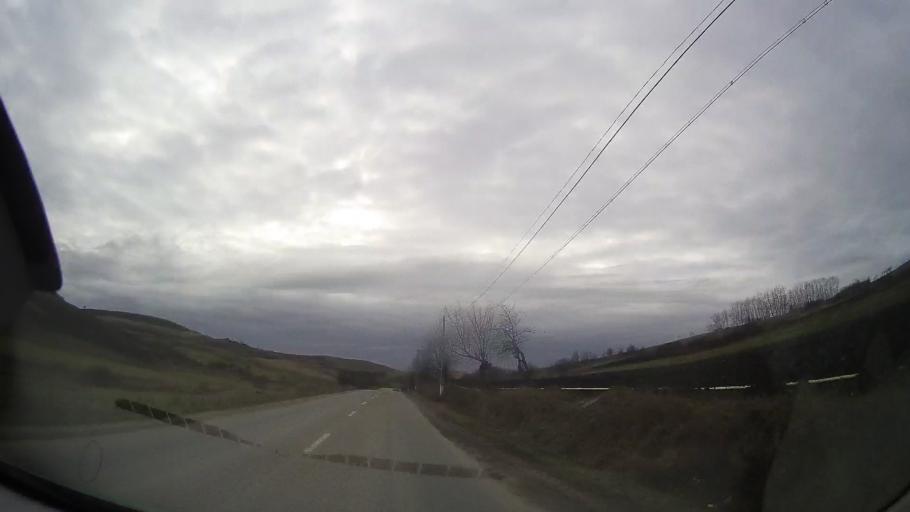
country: RO
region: Bistrita-Nasaud
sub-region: Comuna Budesti
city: Budesti
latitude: 46.8546
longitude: 24.2433
